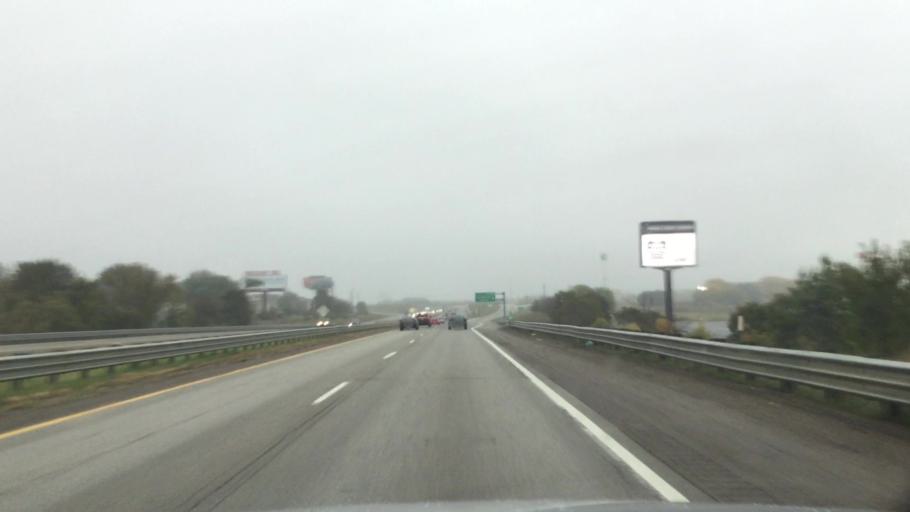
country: US
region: Michigan
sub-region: Kalamazoo County
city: Eastwood
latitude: 42.2542
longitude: -85.5379
